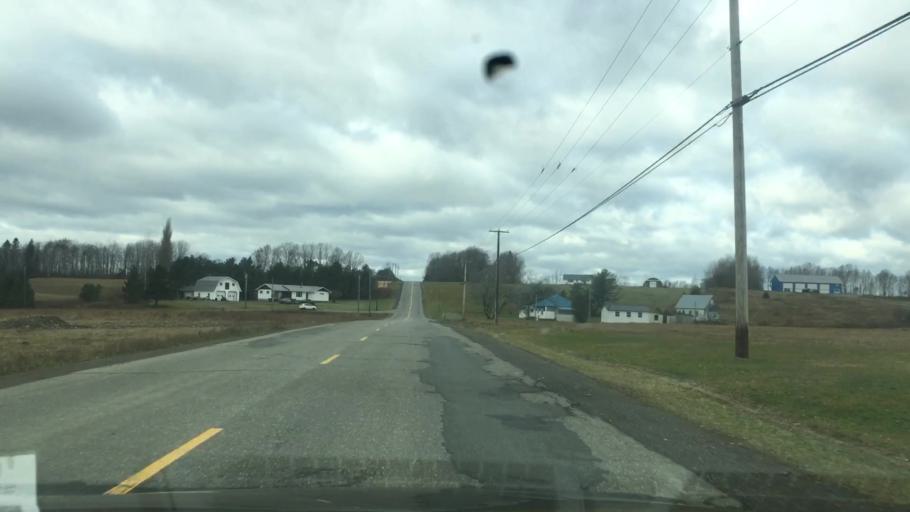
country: US
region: Maine
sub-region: Aroostook County
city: Fort Fairfield
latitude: 46.7586
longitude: -67.7699
